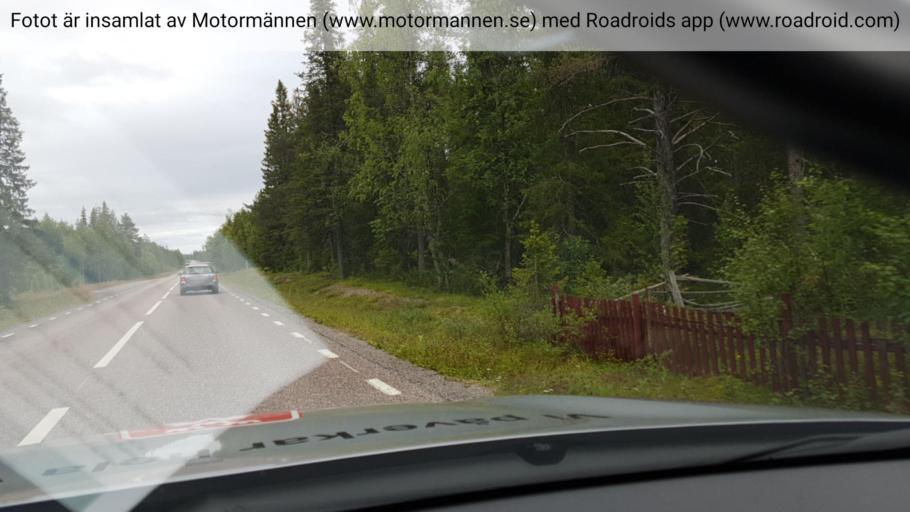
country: SE
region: Norrbotten
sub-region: Gallivare Kommun
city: Gaellivare
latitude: 67.0543
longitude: 21.5924
